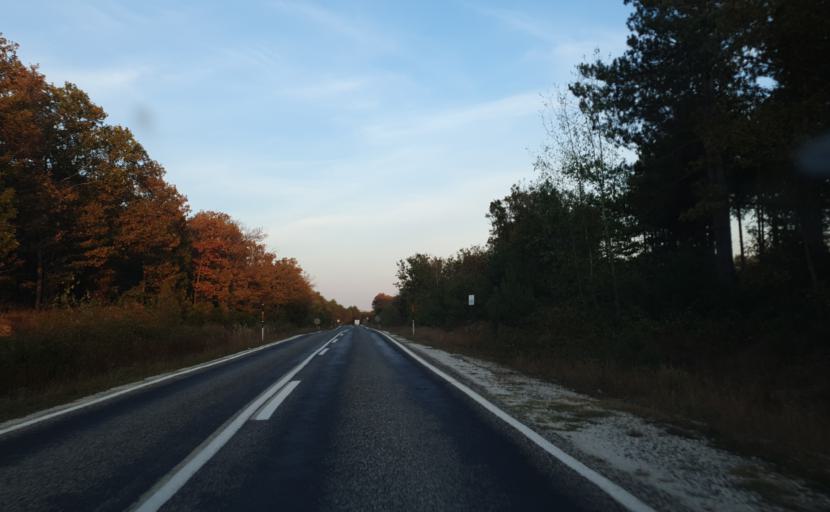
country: TR
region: Kirklareli
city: Igneada
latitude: 41.8676
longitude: 27.8478
